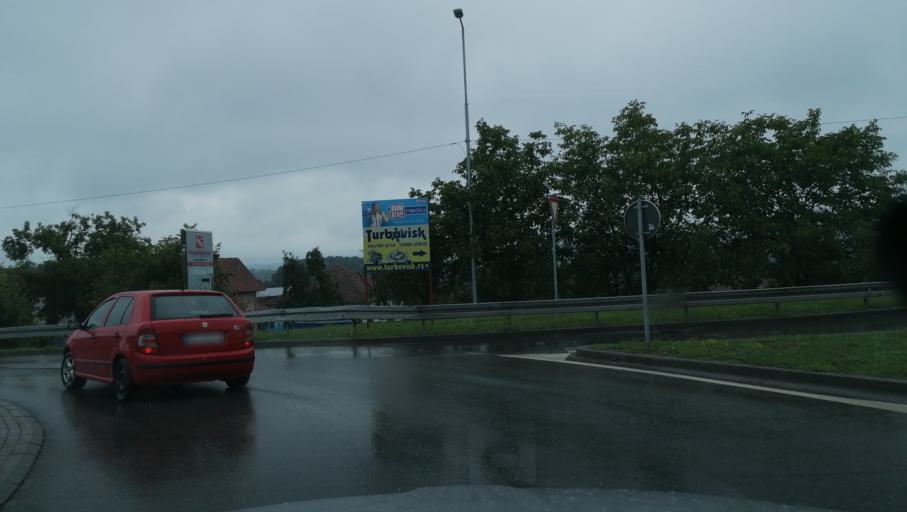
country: RS
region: Central Serbia
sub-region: Raski Okrug
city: Kraljevo
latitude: 43.7372
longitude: 20.6704
